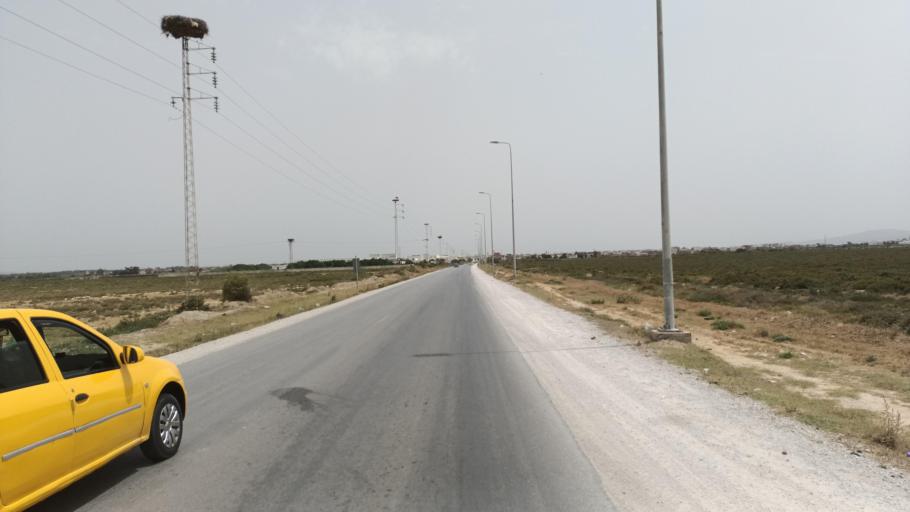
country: TN
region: Nabul
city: Manzil Bu Zalafah
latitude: 36.7168
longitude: 10.4776
